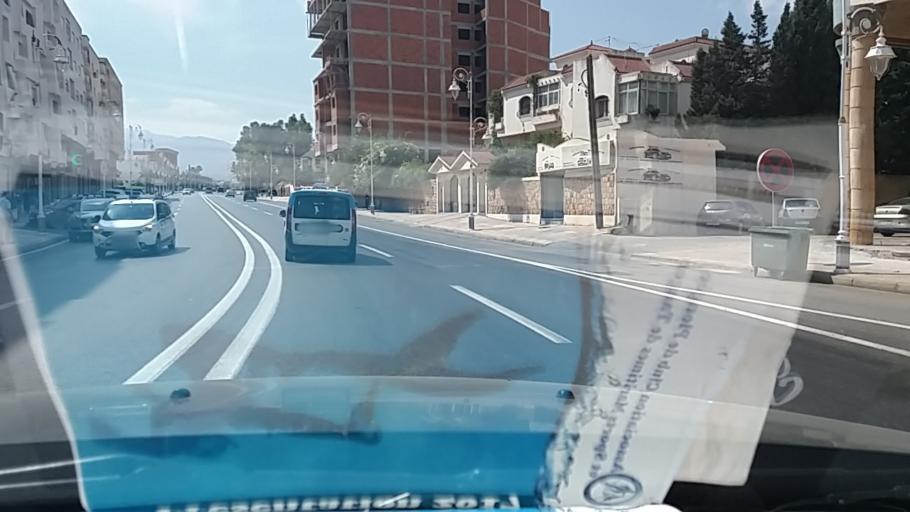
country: MA
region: Tanger-Tetouan
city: Tetouan
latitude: 35.5970
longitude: -5.3398
